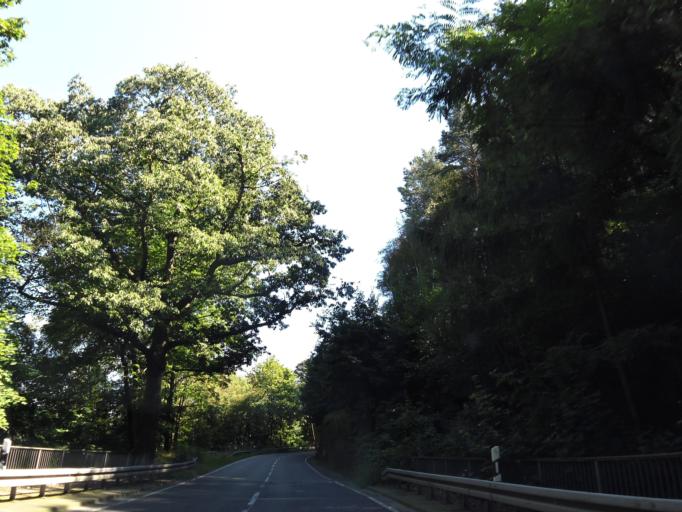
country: DE
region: Saxony
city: Kurort Gohrisch
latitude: 50.9252
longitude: 14.1157
